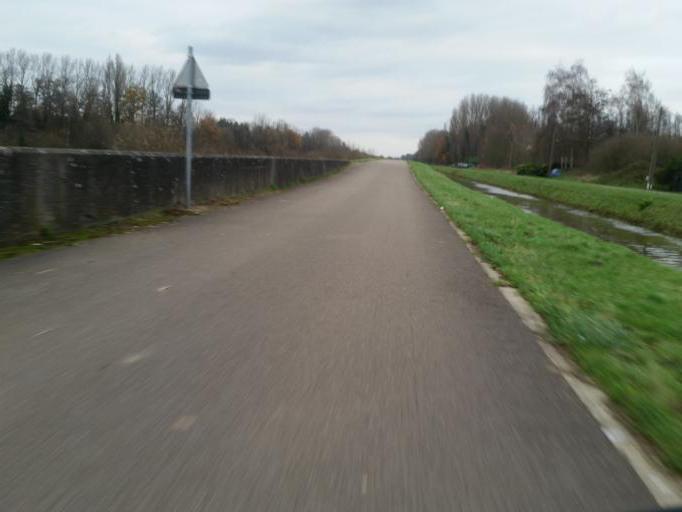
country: BE
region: Flanders
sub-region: Provincie Antwerpen
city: Lier
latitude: 51.1597
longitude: 4.6079
